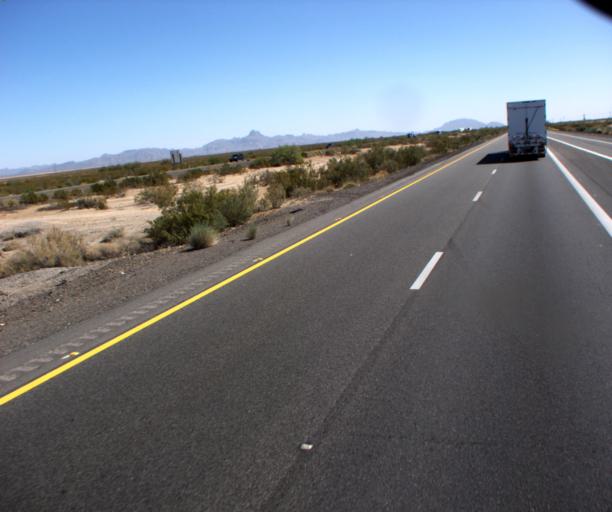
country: US
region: Arizona
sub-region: La Paz County
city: Salome
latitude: 33.5679
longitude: -113.3478
